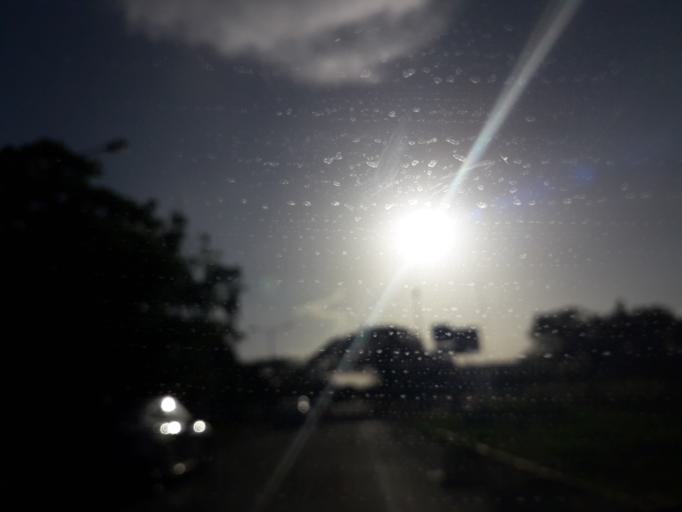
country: MX
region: Yucatan
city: Merida
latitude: 21.0278
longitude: -89.6275
